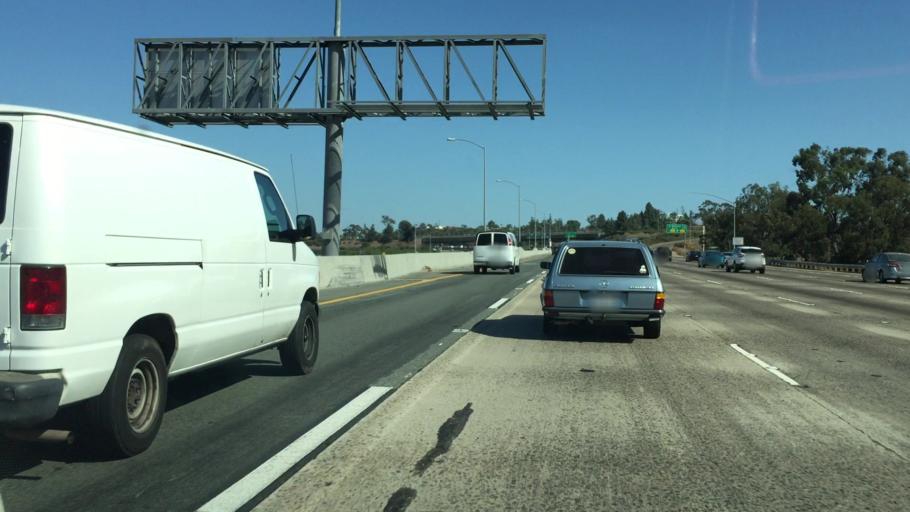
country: US
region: California
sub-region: San Diego County
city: Chula Vista
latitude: 32.6447
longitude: -117.0583
